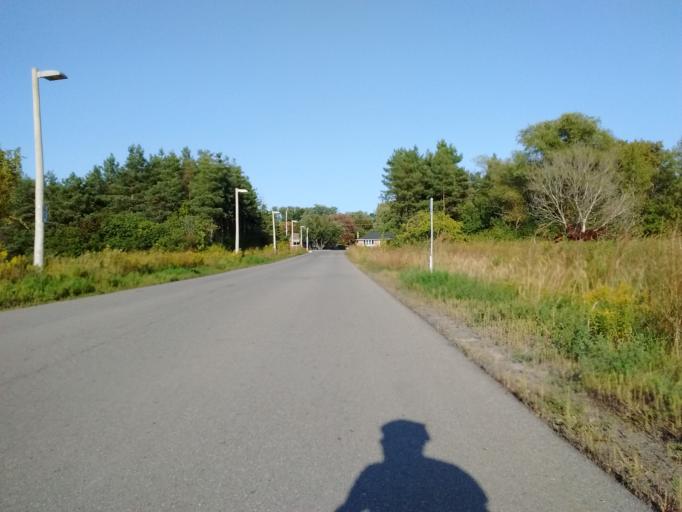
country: CA
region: Ontario
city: Ottawa
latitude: 45.4404
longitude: -75.6139
